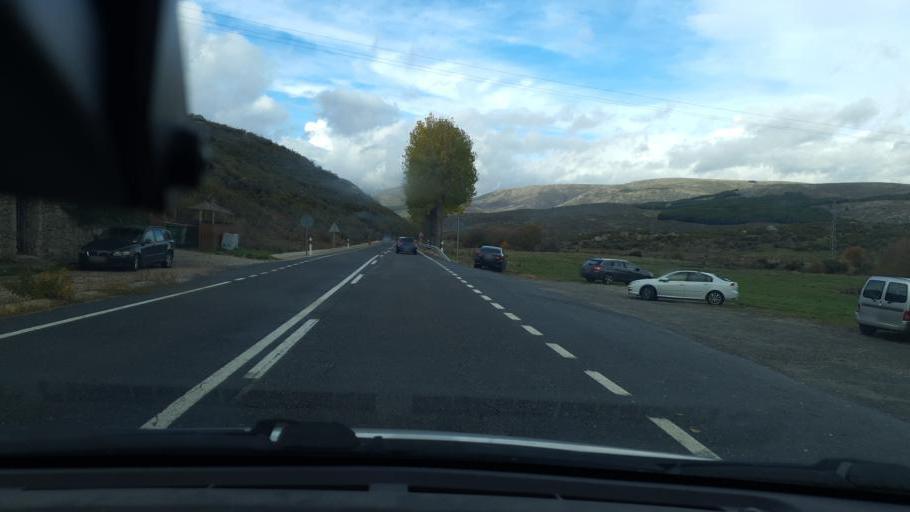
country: ES
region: Castille and Leon
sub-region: Provincia de Avila
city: San Martin del Pimpollar
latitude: 40.3623
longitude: -5.0153
